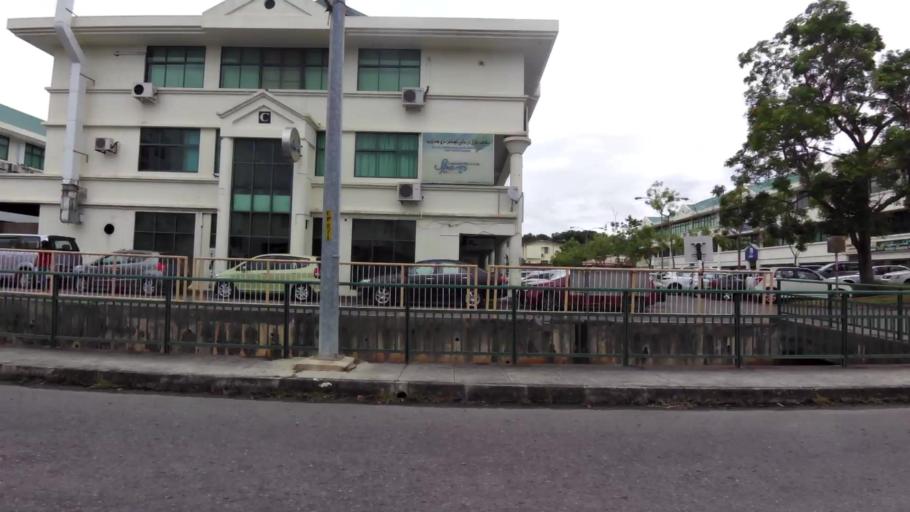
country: BN
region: Brunei and Muara
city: Bandar Seri Begawan
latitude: 4.8962
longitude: 114.9204
